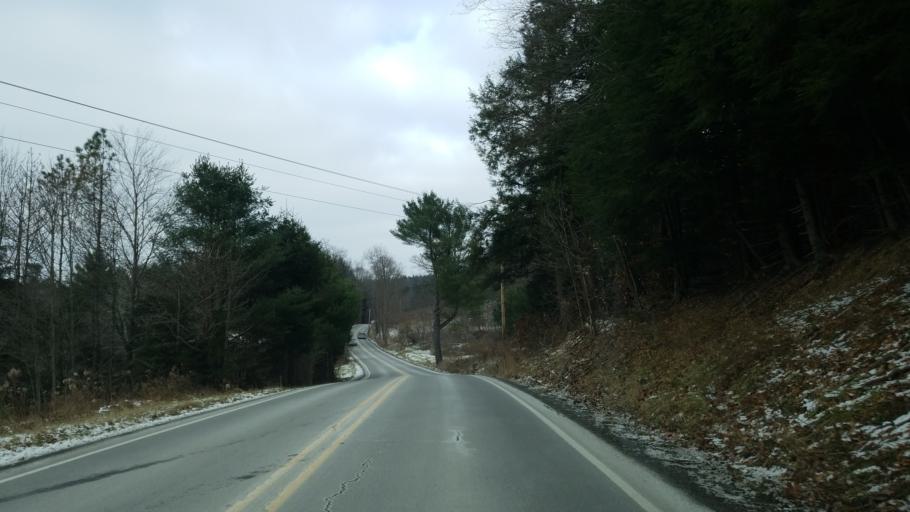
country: US
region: Pennsylvania
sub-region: Clearfield County
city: DuBois
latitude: 41.0941
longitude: -78.7333
